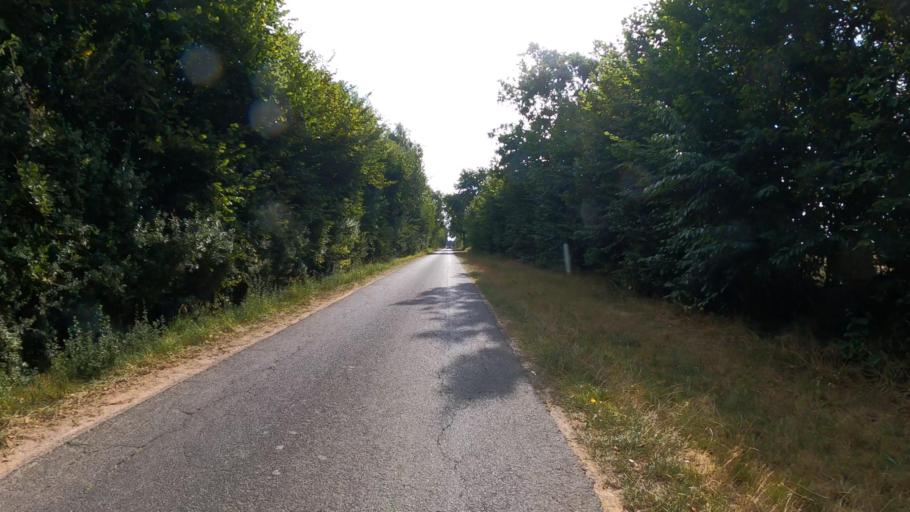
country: DE
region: Schleswig-Holstein
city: Hamwarde
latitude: 53.4523
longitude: 10.4105
